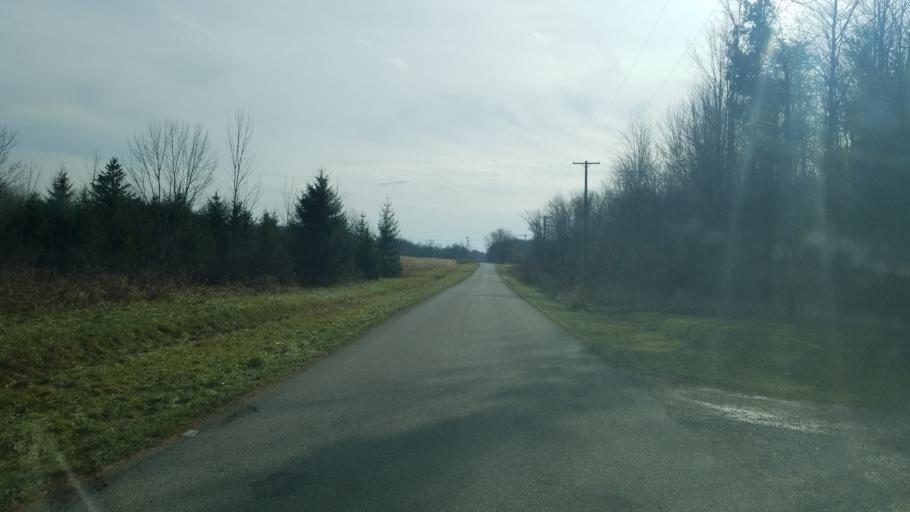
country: US
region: Ohio
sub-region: Ashtabula County
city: Roaming Shores
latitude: 41.6816
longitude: -80.9299
